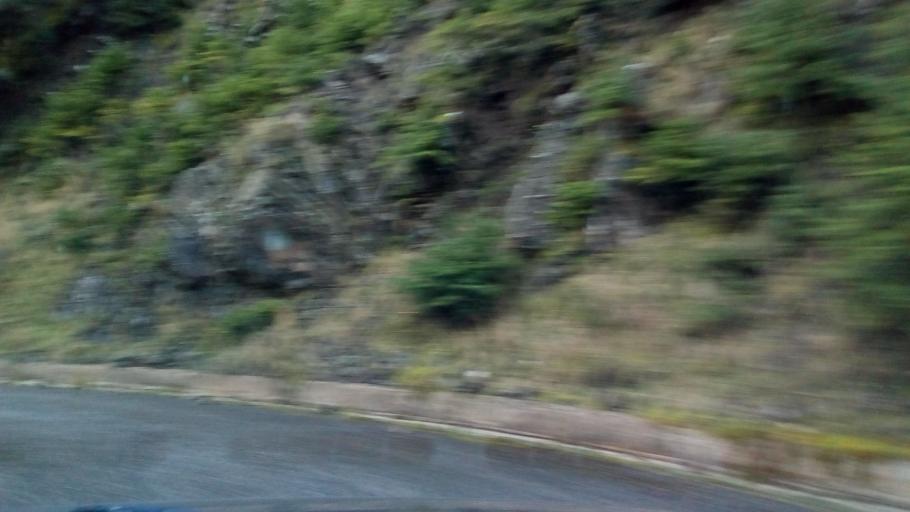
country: GR
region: West Greece
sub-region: Nomos Aitolias kai Akarnanias
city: Nafpaktos
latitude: 38.5346
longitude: 21.8462
